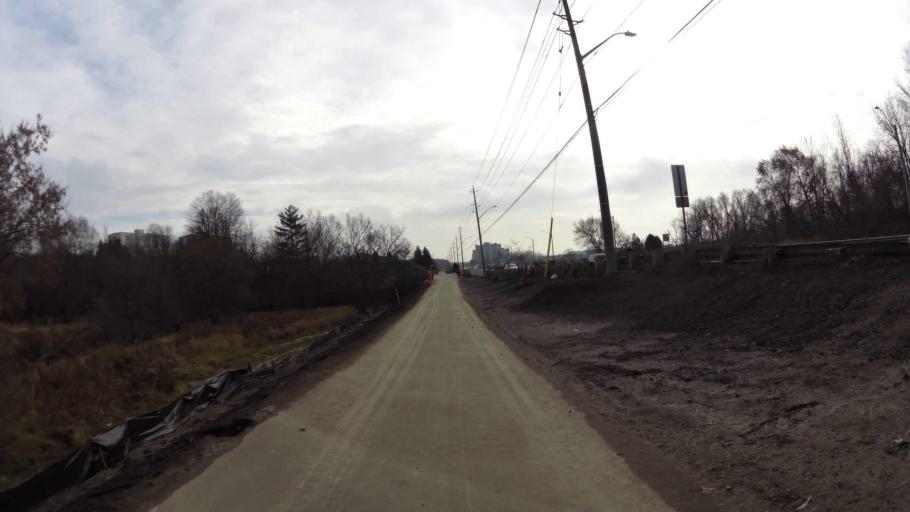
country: CA
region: Ontario
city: Kitchener
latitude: 43.3989
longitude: -80.4363
